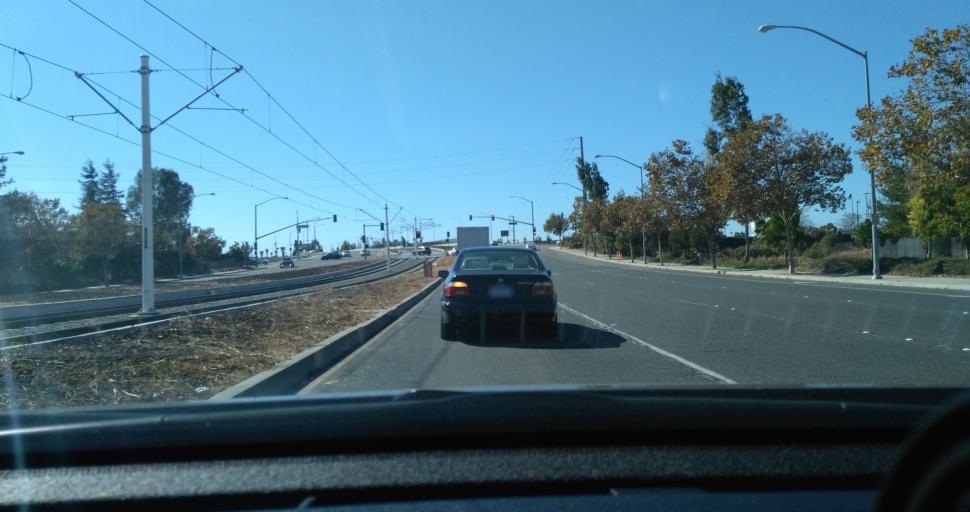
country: US
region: California
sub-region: Santa Clara County
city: Milpitas
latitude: 37.4159
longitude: -121.9089
